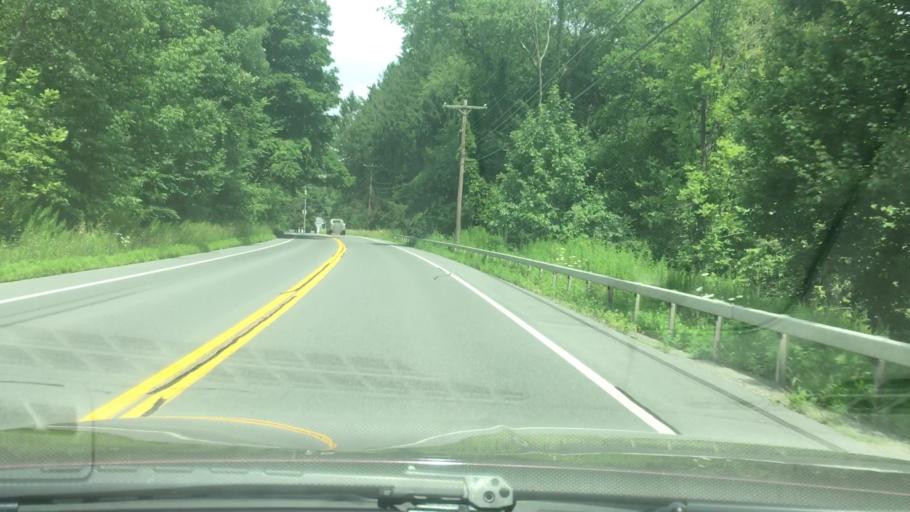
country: US
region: New York
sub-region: Dutchess County
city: Pawling
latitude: 41.6176
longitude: -73.6769
